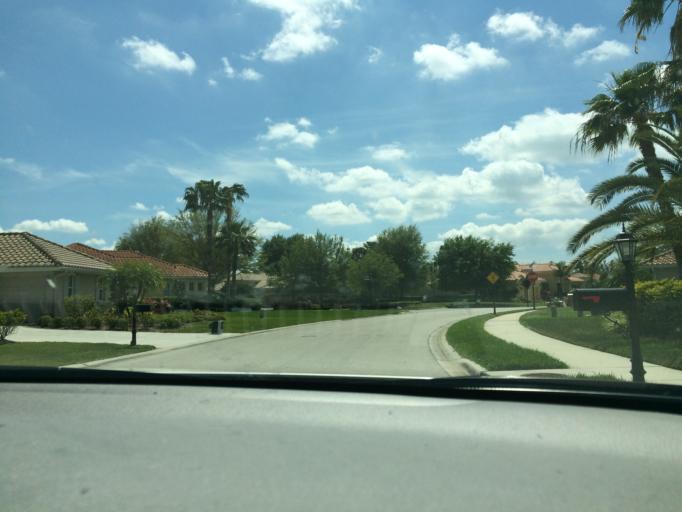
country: US
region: Florida
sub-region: Manatee County
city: Ellenton
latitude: 27.5081
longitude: -82.4423
